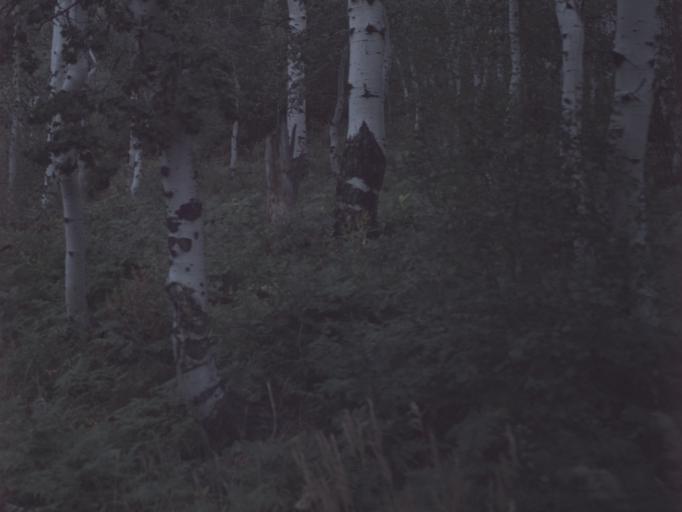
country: US
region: Utah
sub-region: Utah County
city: Lindon
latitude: 40.4157
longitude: -111.6074
